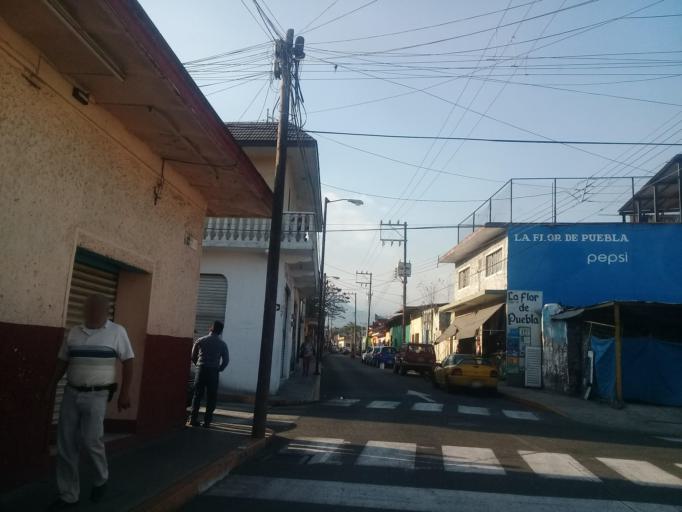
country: MX
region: Veracruz
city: Orizaba
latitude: 18.8531
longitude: -97.1090
